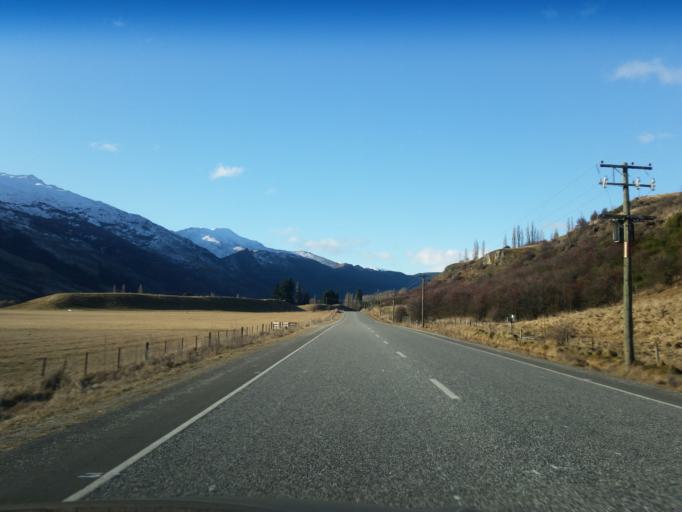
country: NZ
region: Otago
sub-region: Queenstown-Lakes District
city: Queenstown
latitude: -44.9650
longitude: 168.7133
